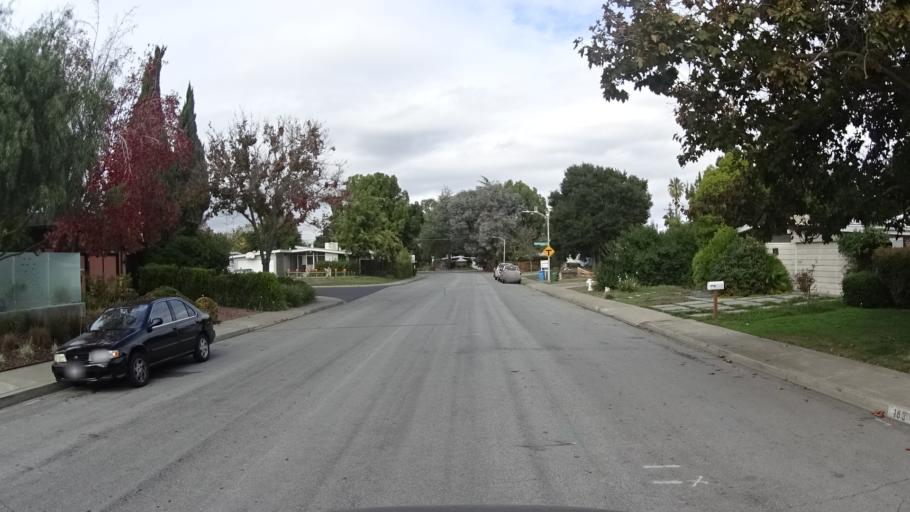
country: US
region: California
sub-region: Santa Clara County
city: Cupertino
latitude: 37.3261
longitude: -121.9916
